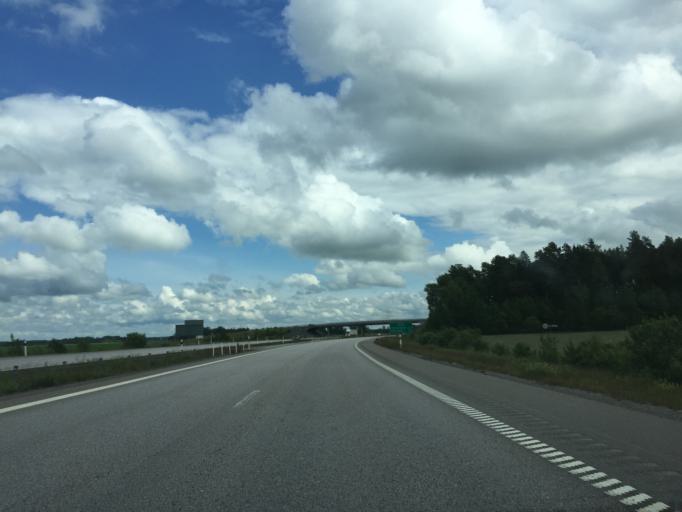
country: SE
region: Vaestmanland
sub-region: Arboga Kommun
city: Arboga
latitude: 59.4194
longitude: 15.7775
